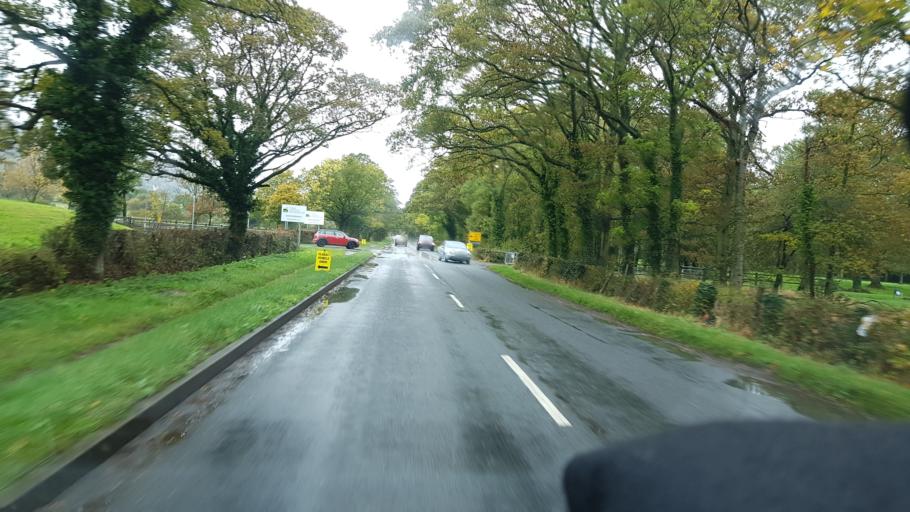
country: GB
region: England
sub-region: Worcestershire
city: Great Malvern
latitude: 52.0853
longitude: -2.3095
